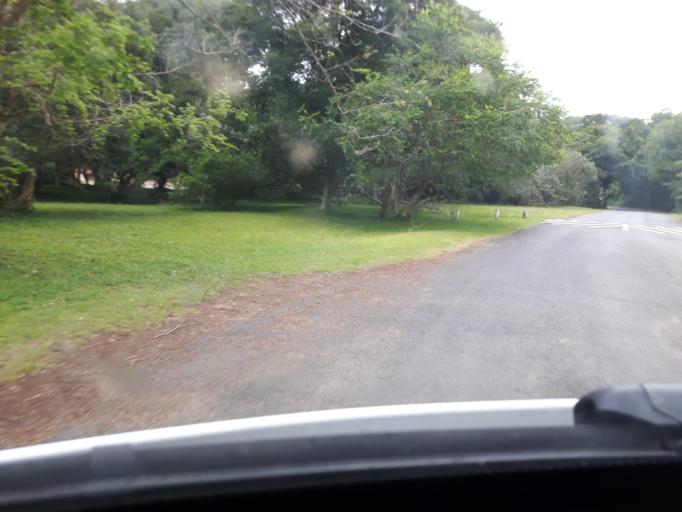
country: ZA
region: KwaZulu-Natal
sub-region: uMkhanyakude District Municipality
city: Mtubatuba
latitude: -28.3818
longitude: 32.4116
